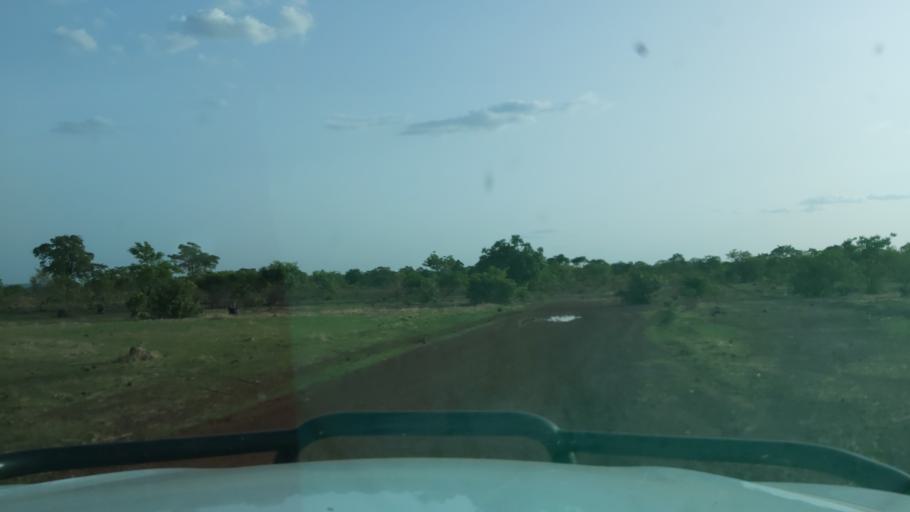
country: ML
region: Koulikoro
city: Kolokani
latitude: 13.2140
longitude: -7.8984
